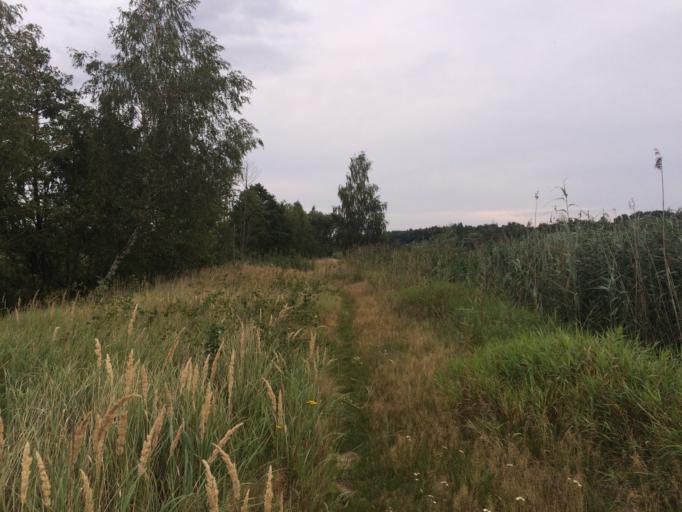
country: PL
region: Swietokrzyskie
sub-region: Powiat starachowicki
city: Starachowice
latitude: 51.0513
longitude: 21.0548
